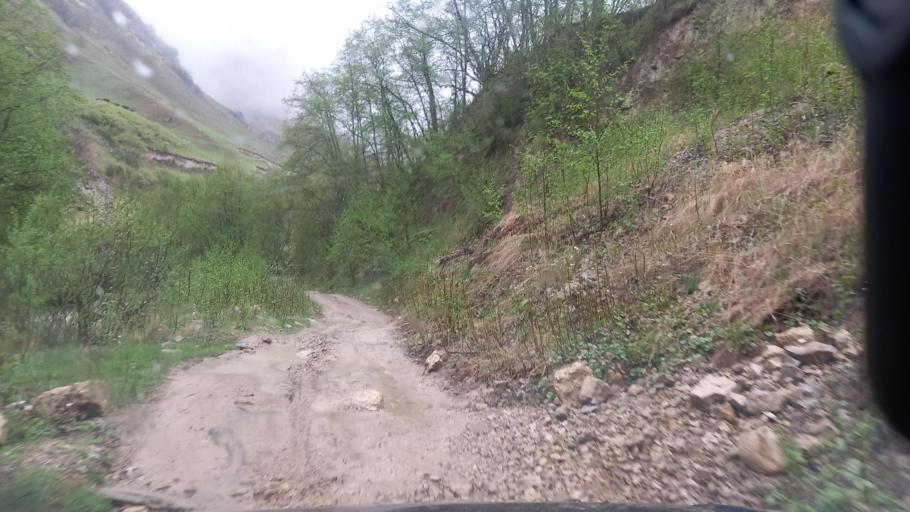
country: RU
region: Kabardino-Balkariya
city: Bylym
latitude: 43.5996
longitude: 42.9246
